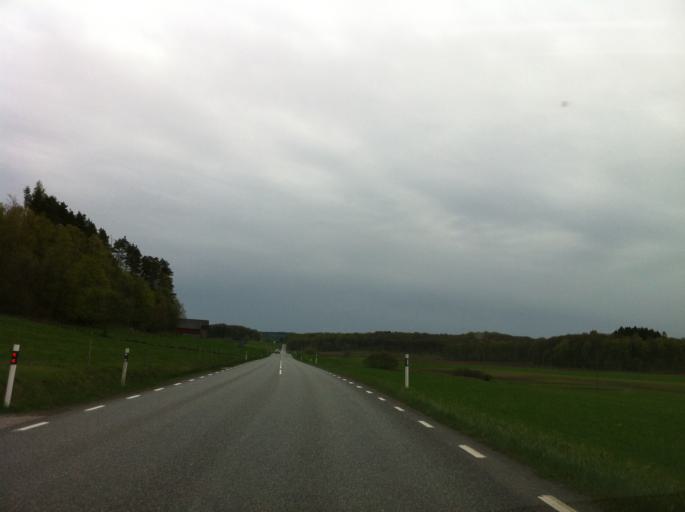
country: SE
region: Halland
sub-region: Falkenbergs Kommun
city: Falkenberg
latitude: 57.0478
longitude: 12.6086
